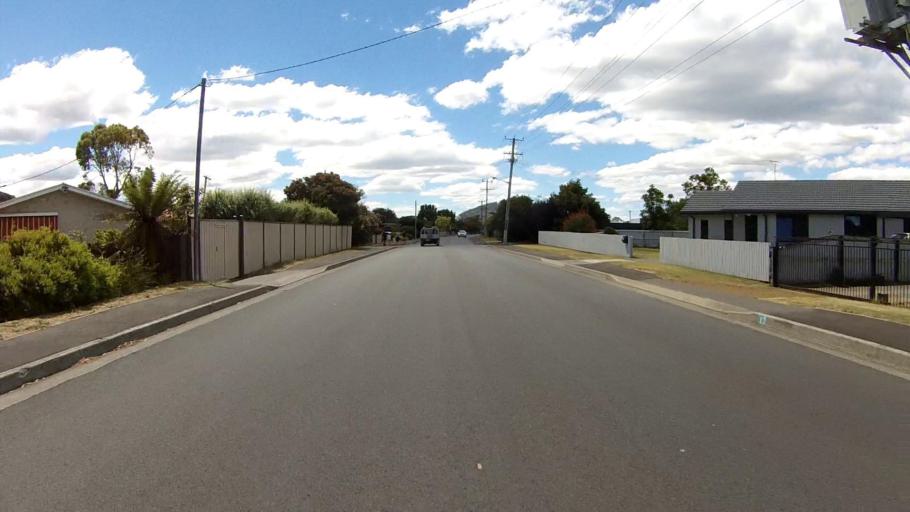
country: AU
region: Tasmania
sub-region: Clarence
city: Lauderdale
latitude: -42.9077
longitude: 147.4925
